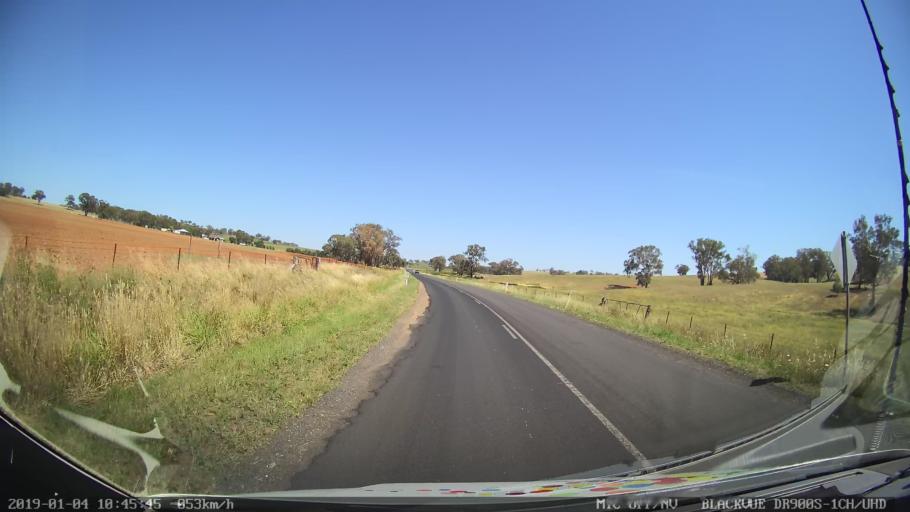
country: AU
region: New South Wales
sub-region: Cabonne
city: Molong
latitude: -33.2868
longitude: 148.7284
